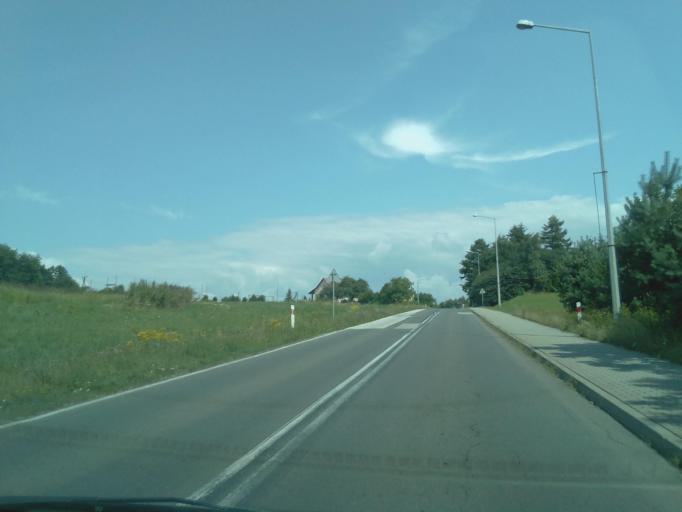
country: PL
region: Subcarpathian Voivodeship
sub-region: Powiat ropczycko-sedziszowski
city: Ropczyce
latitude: 50.0610
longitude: 21.5973
